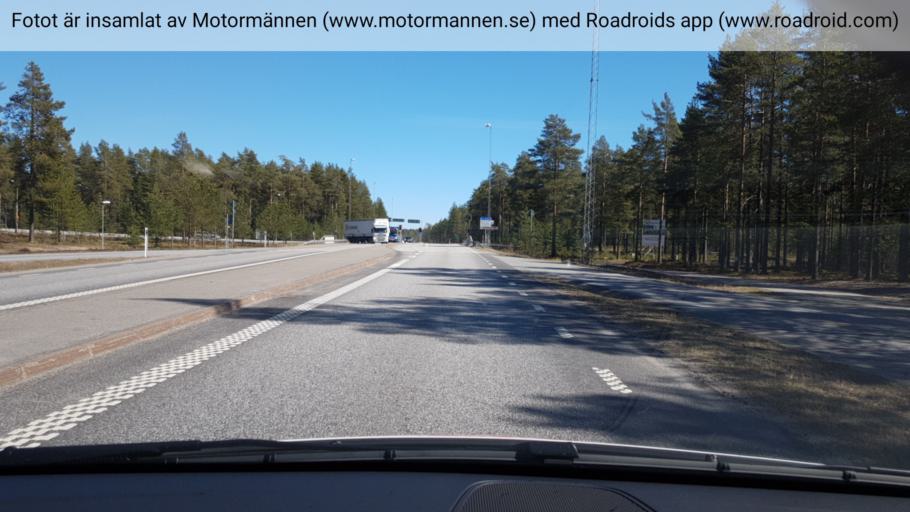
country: SE
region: Vaesterbotten
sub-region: Umea Kommun
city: Roback
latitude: 63.8458
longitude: 20.1574
